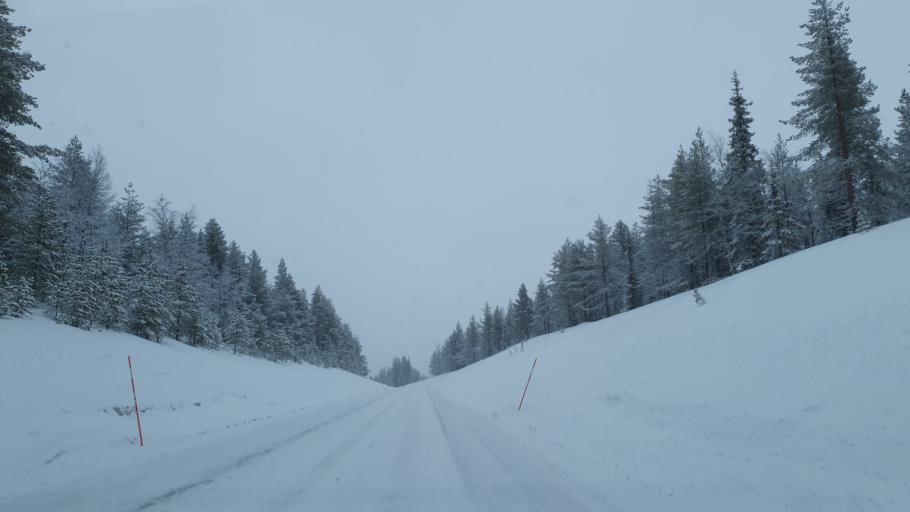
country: FI
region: Lapland
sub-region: Tunturi-Lappi
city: Kittilae
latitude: 67.6494
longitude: 24.6556
